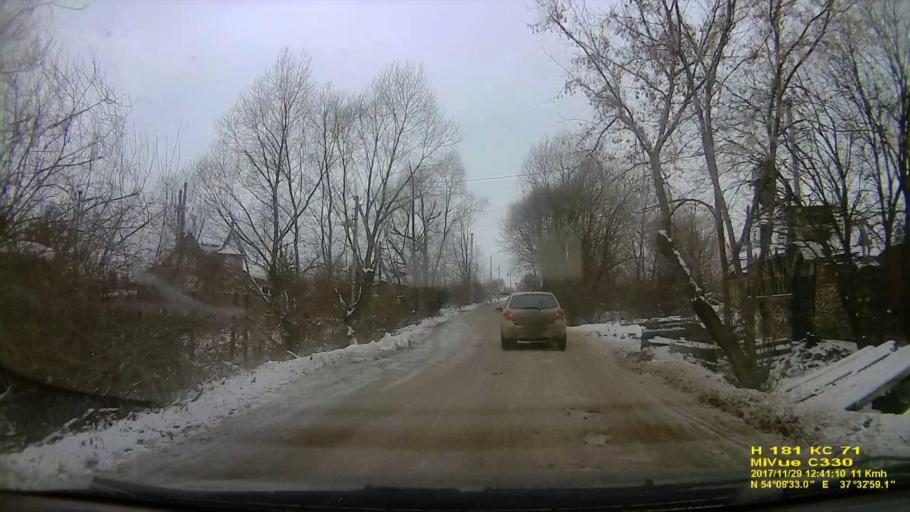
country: RU
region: Tula
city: Kosaya Gora
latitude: 54.1592
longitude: 37.5498
